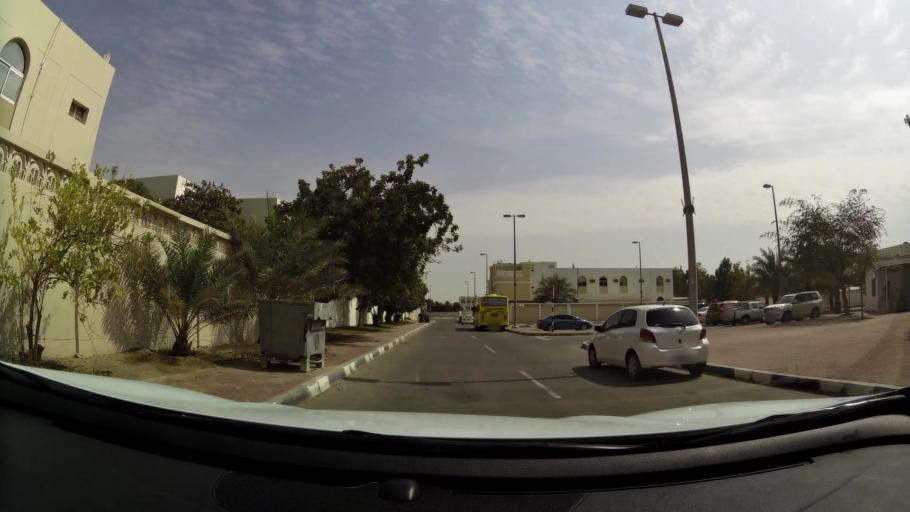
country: AE
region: Abu Dhabi
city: Abu Dhabi
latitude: 24.5446
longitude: 54.6719
